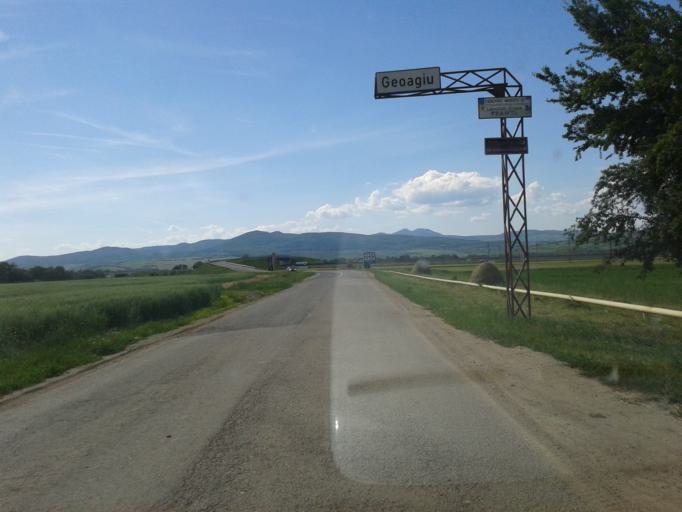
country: RO
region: Hunedoara
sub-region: Comuna Geoagiu
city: Geoagiu
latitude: 45.8847
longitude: 23.2476
